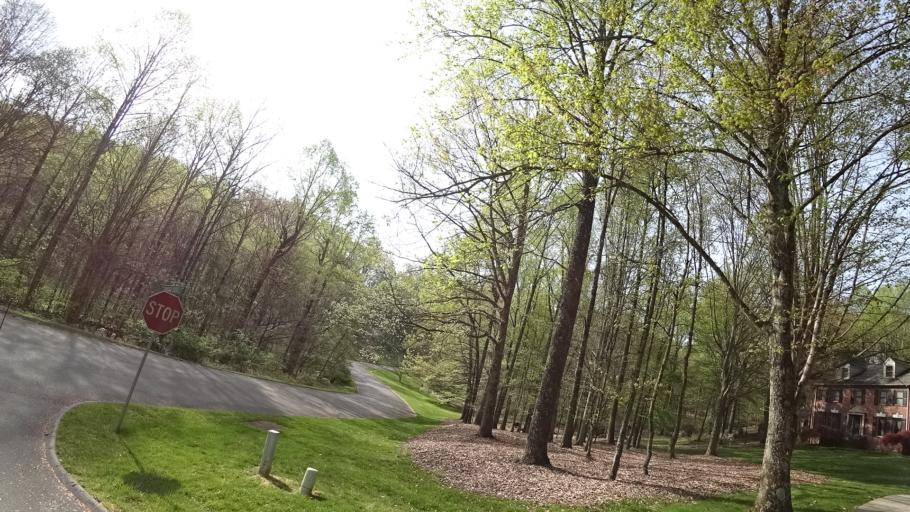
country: US
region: Tennessee
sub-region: Knox County
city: Knoxville
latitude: 35.9038
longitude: -83.9888
